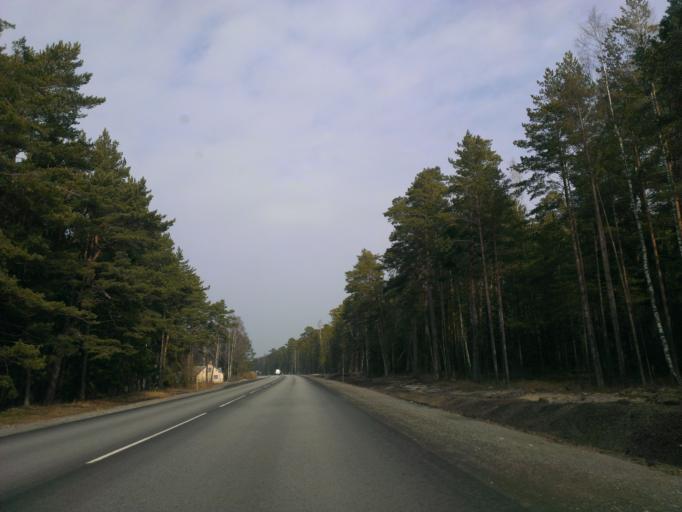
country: LV
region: Salacgrivas
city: Ainazi
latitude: 57.8174
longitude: 24.3471
